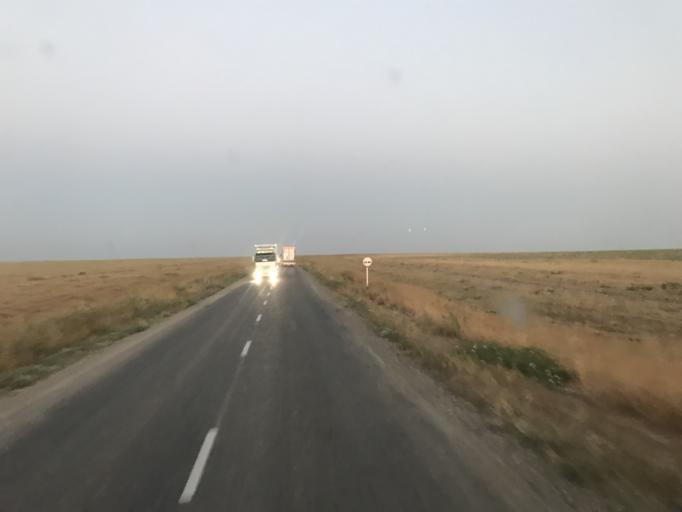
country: UZ
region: Toshkent
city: Chinoz
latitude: 41.1887
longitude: 68.6244
